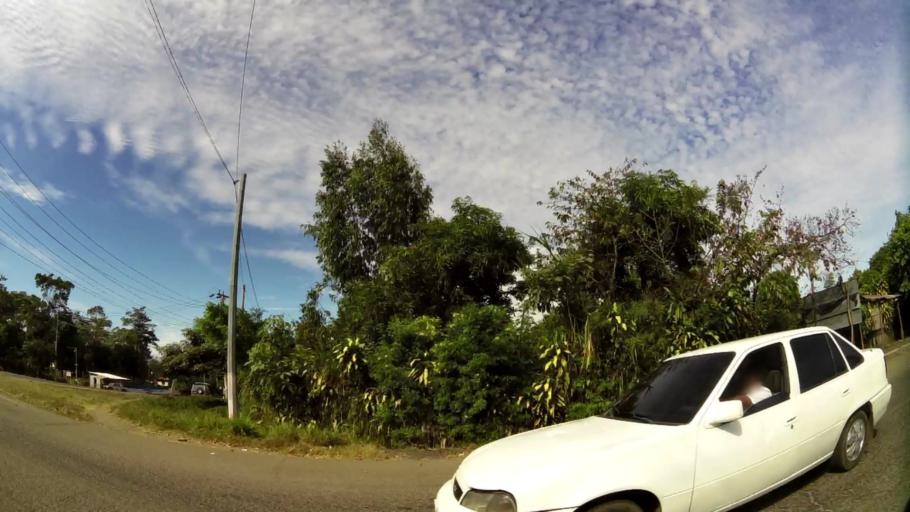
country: SV
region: Santa Ana
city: Chalchuapa
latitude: 13.9775
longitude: -89.6902
